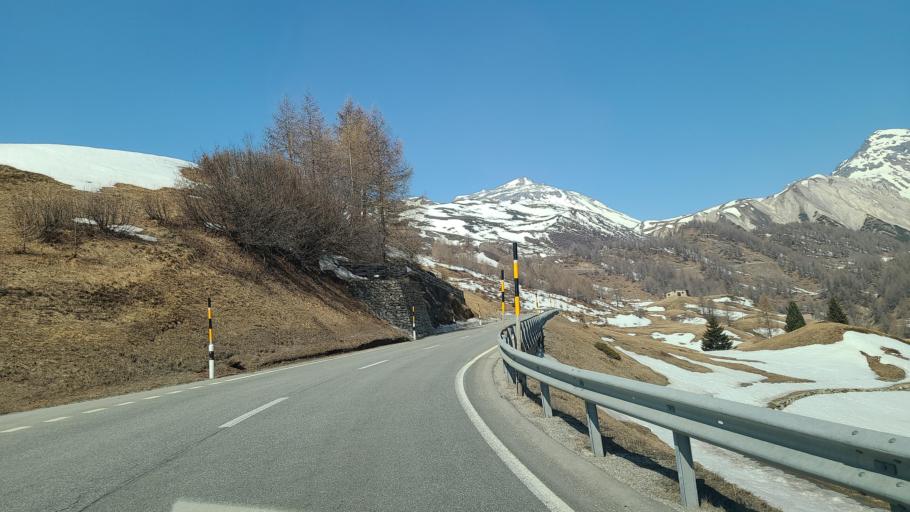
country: CH
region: Grisons
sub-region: Bernina District
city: Poschiavo
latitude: 46.4090
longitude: 10.0569
